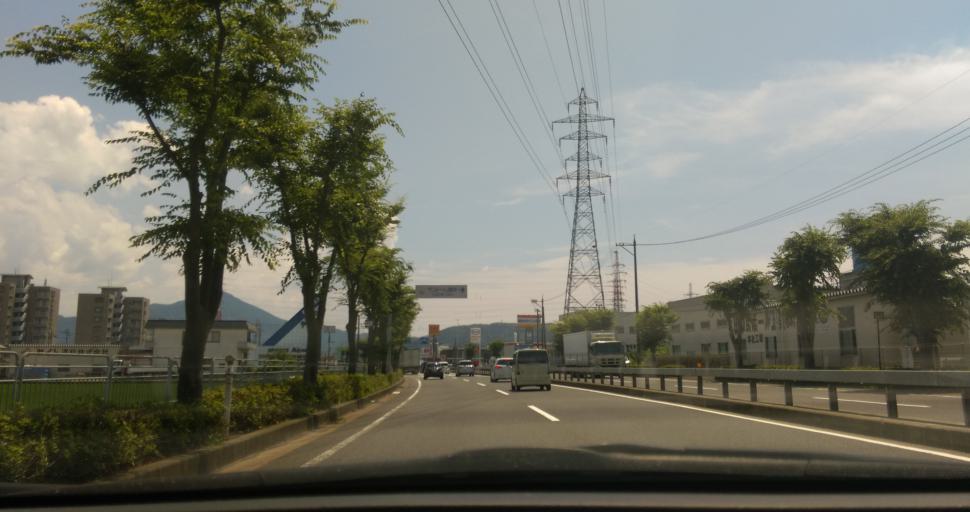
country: JP
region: Fukui
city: Sabae
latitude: 35.9346
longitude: 136.1898
